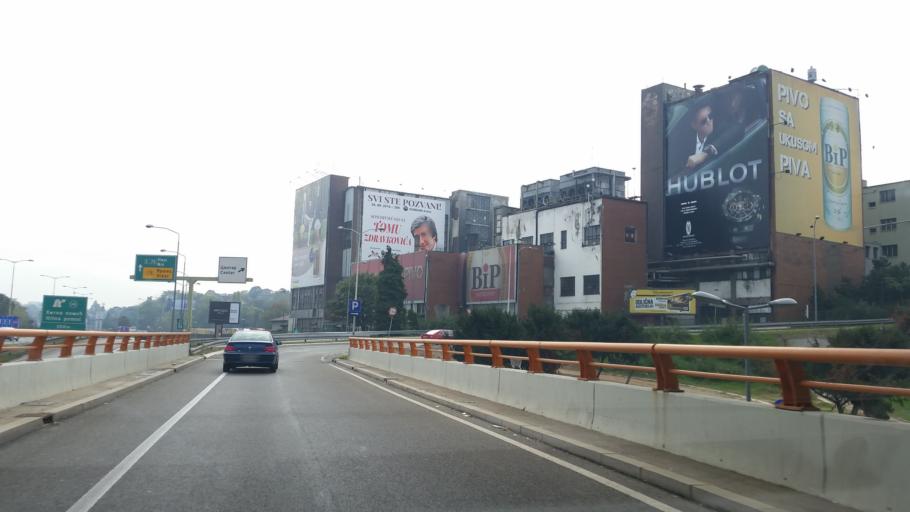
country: RS
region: Central Serbia
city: Belgrade
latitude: 44.7975
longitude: 20.4502
